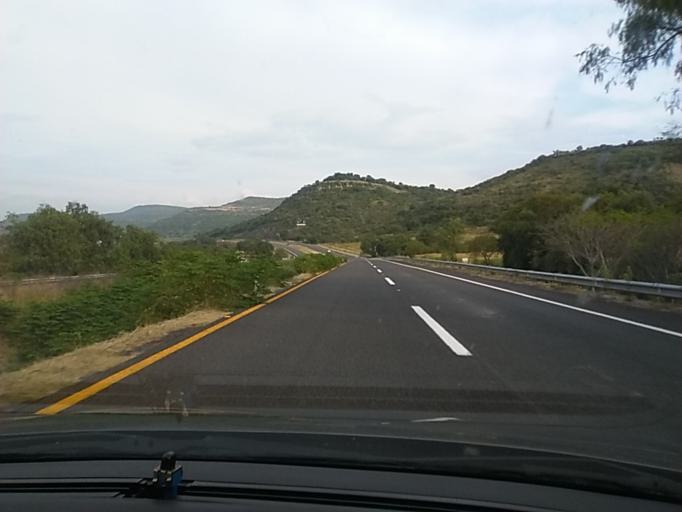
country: MX
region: Michoacan
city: Copandaro de Galeana
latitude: 19.8847
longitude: -101.2256
